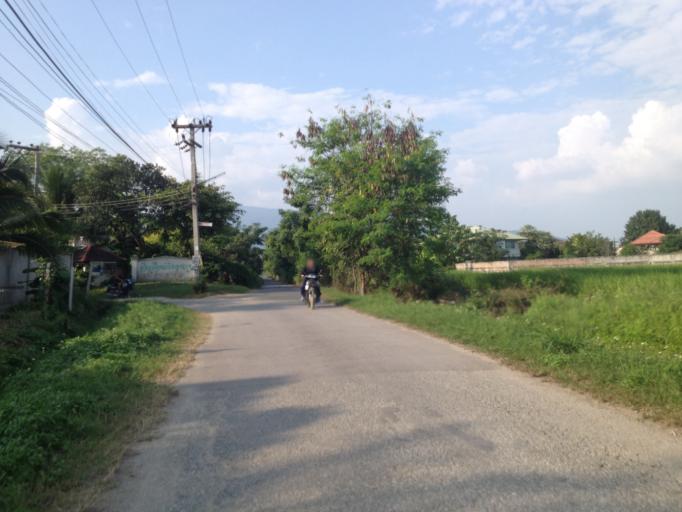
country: TH
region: Chiang Mai
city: Hang Dong
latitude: 18.7285
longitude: 98.9298
